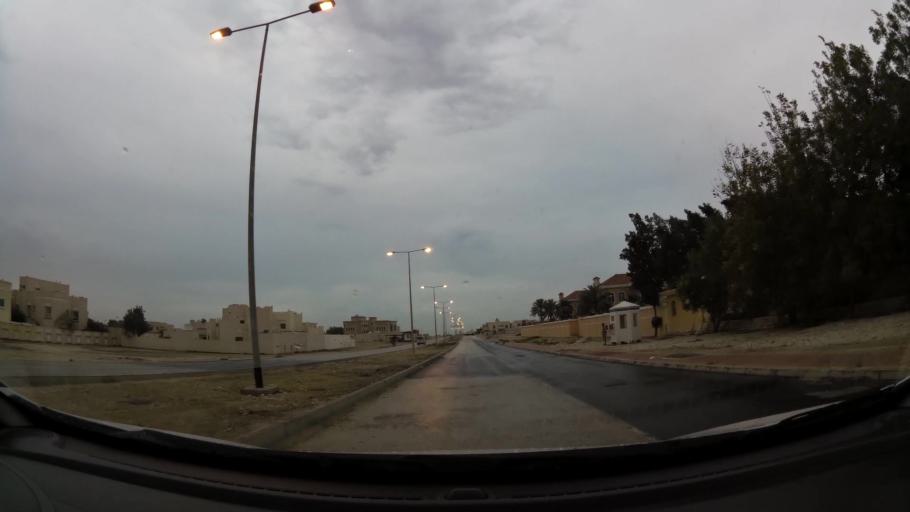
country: BH
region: Central Governorate
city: Madinat Hamad
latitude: 26.1428
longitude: 50.5171
